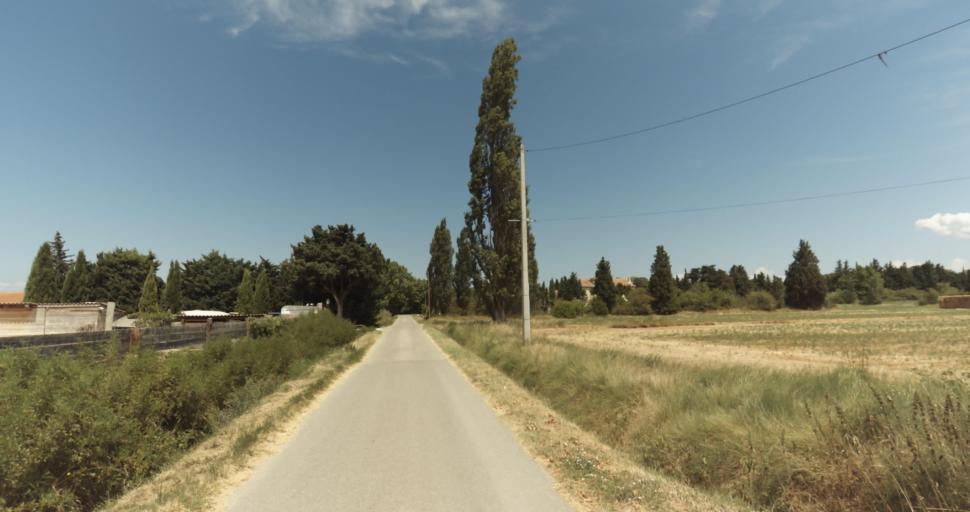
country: FR
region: Provence-Alpes-Cote d'Azur
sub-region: Departement du Vaucluse
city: Monteux
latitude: 44.0359
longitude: 4.9809
